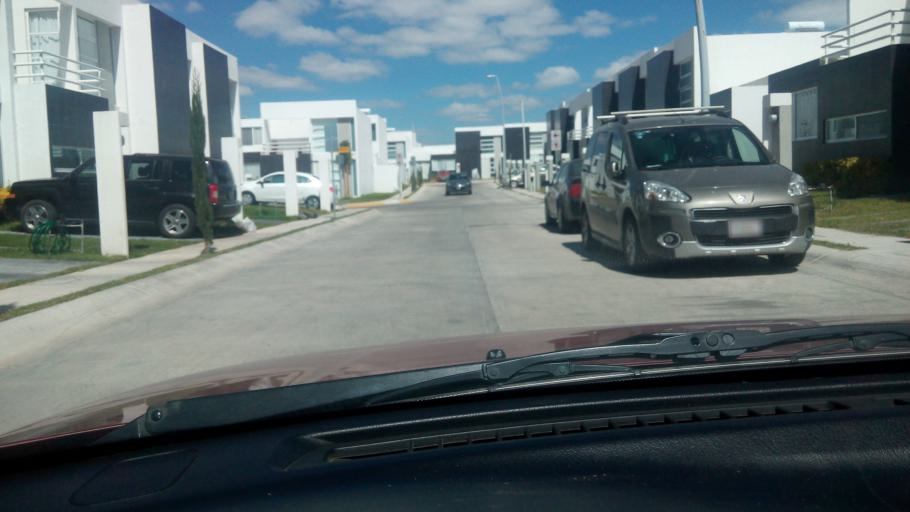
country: MX
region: Aguascalientes
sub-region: Aguascalientes
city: San Sebastian [Fraccionamiento]
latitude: 21.8285
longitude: -102.3003
